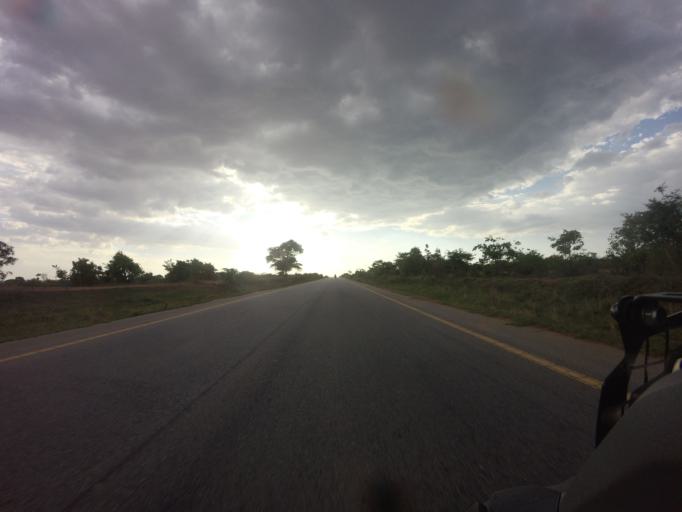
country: AO
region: Huila
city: Lubango
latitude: -14.6019
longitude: 14.0423
